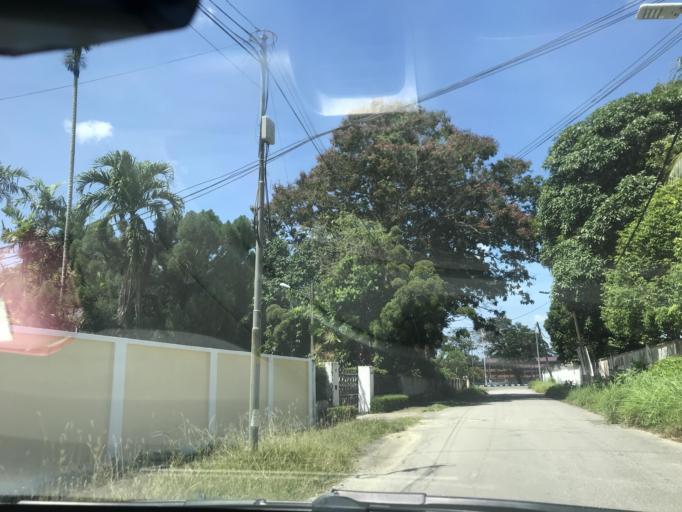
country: MY
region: Kelantan
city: Kota Bharu
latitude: 6.1092
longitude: 102.2526
